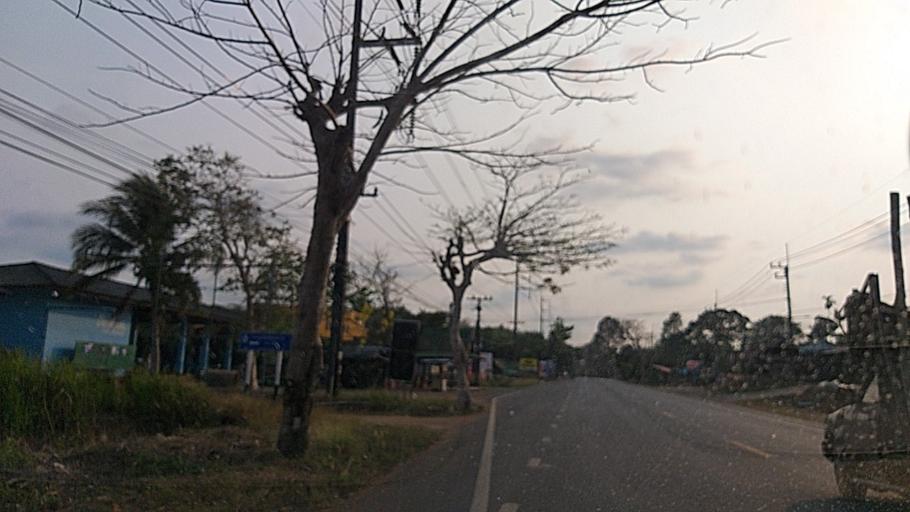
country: TH
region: Trat
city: Khao Saming
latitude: 12.3201
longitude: 102.3608
